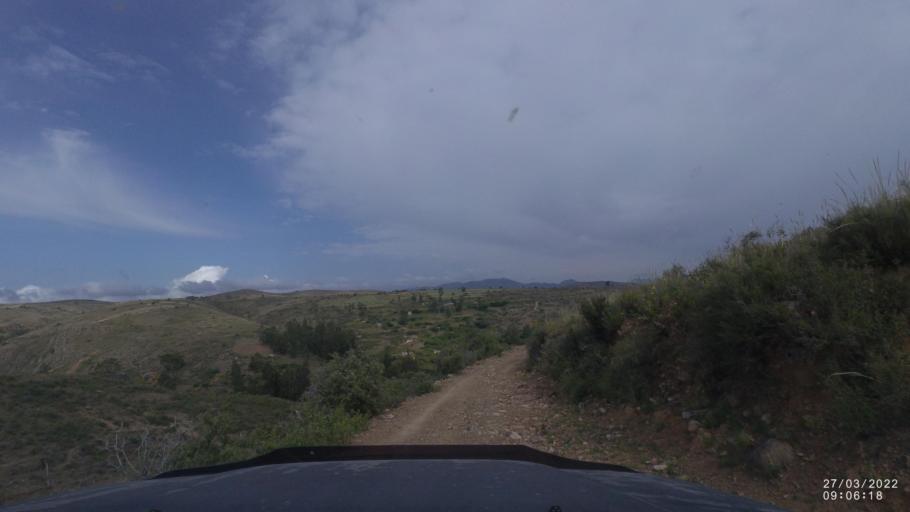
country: BO
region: Cochabamba
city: Cliza
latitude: -17.7319
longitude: -65.8712
